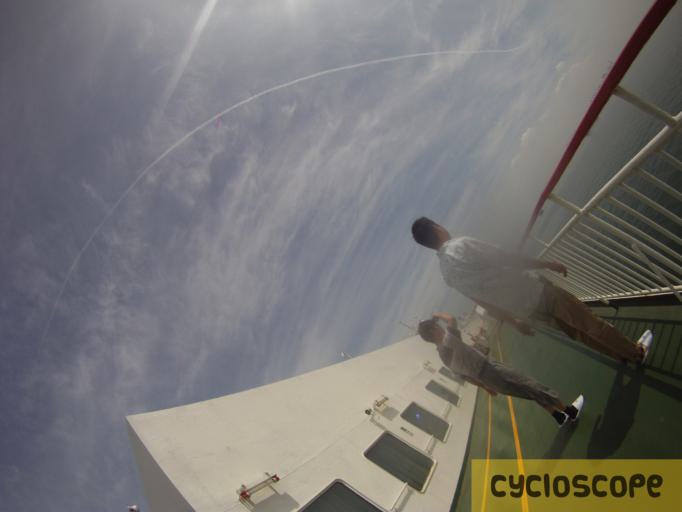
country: KR
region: Incheon
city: Incheon
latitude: 37.3981
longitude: 126.5573
